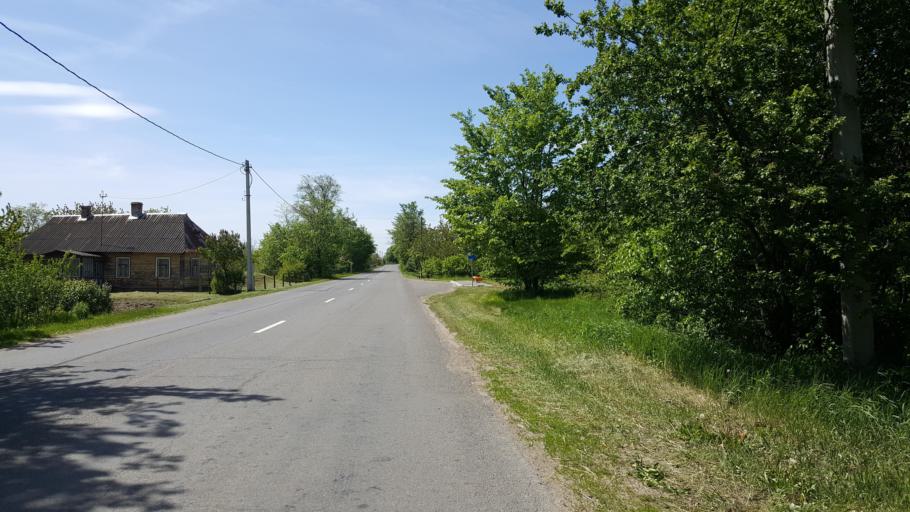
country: BY
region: Brest
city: Kobryn
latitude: 52.3470
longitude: 24.2069
